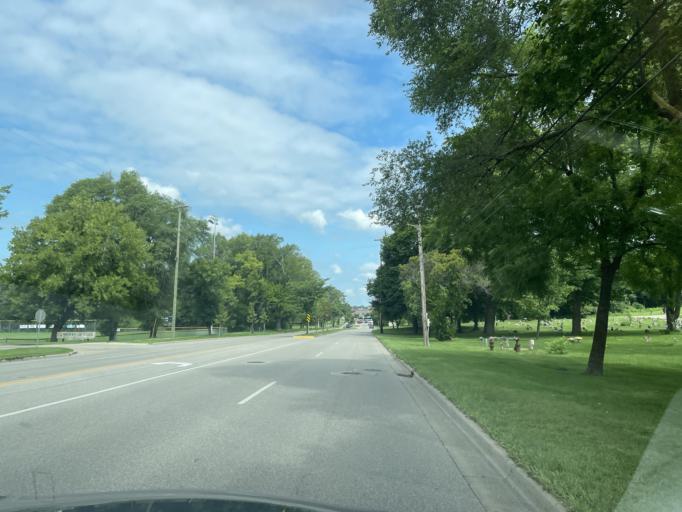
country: US
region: Michigan
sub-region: Kent County
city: East Grand Rapids
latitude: 42.9170
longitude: -85.6309
